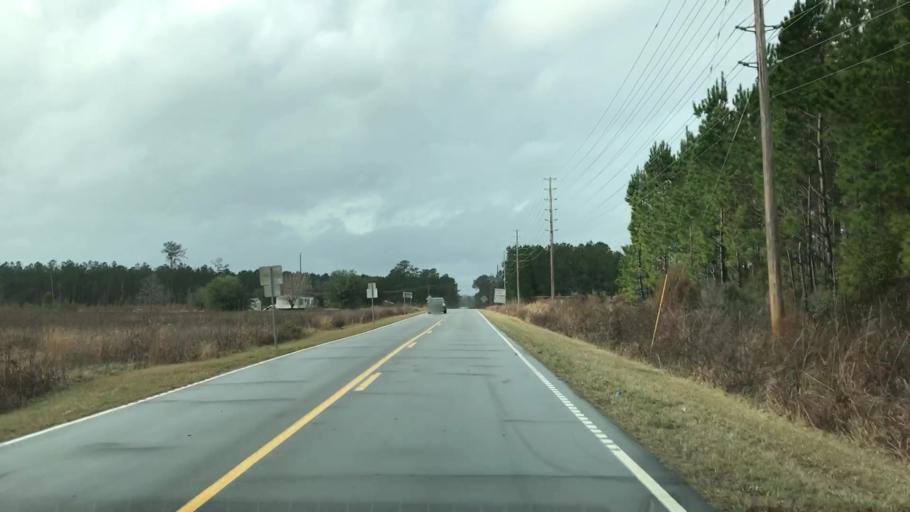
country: US
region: South Carolina
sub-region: Florence County
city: Johnsonville
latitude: 33.6708
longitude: -79.3185
